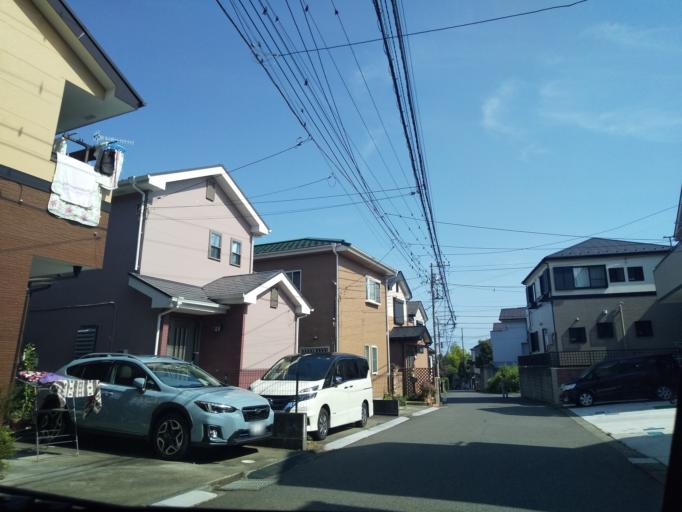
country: JP
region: Kanagawa
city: Minami-rinkan
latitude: 35.4615
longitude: 139.4185
